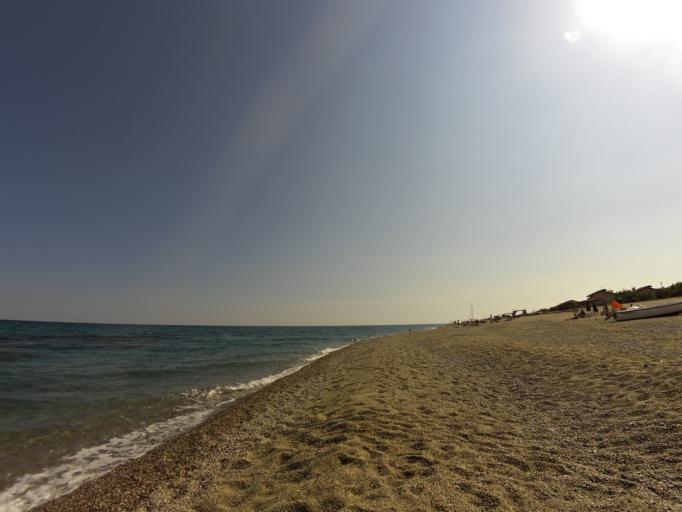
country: IT
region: Calabria
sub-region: Provincia di Reggio Calabria
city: Riace Marina
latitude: 38.4005
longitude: 16.5437
